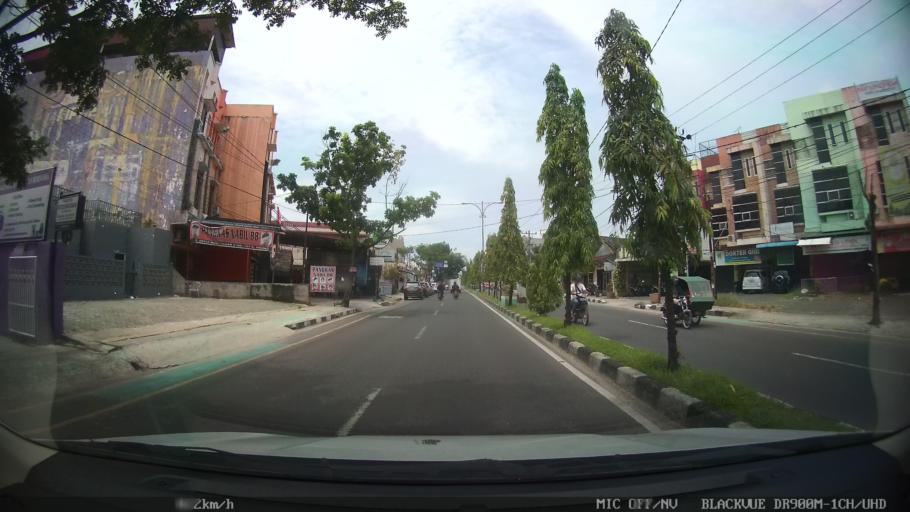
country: ID
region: North Sumatra
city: Sunggal
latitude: 3.5546
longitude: 98.6325
